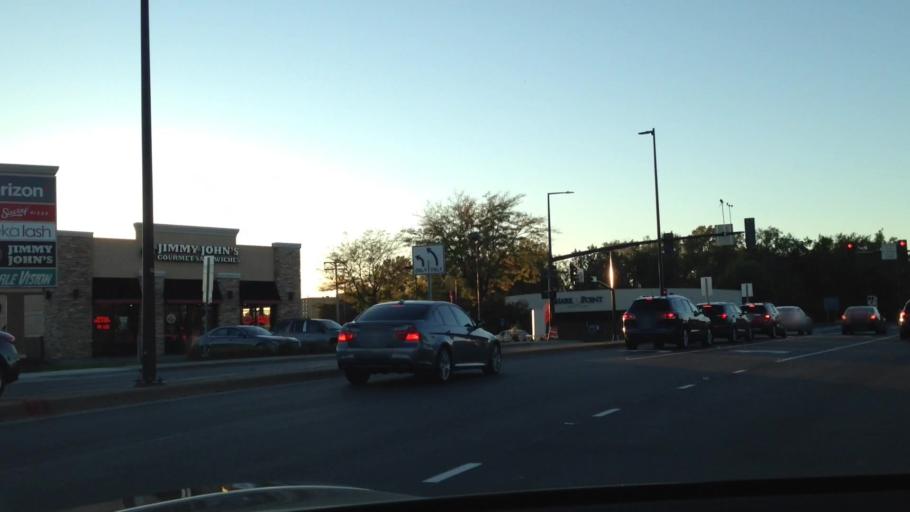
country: US
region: Minnesota
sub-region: Hennepin County
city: Saint Louis Park
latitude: 44.9361
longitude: -93.3867
